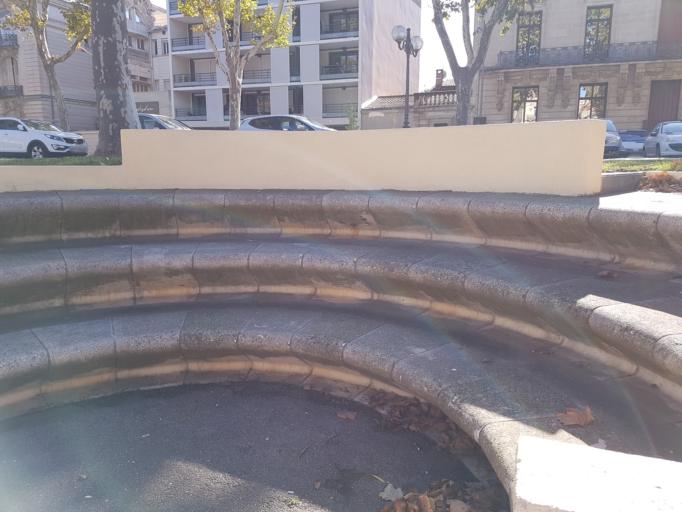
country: FR
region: Languedoc-Roussillon
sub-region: Departement de l'Aude
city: Narbonne
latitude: 43.1802
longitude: 3.0102
